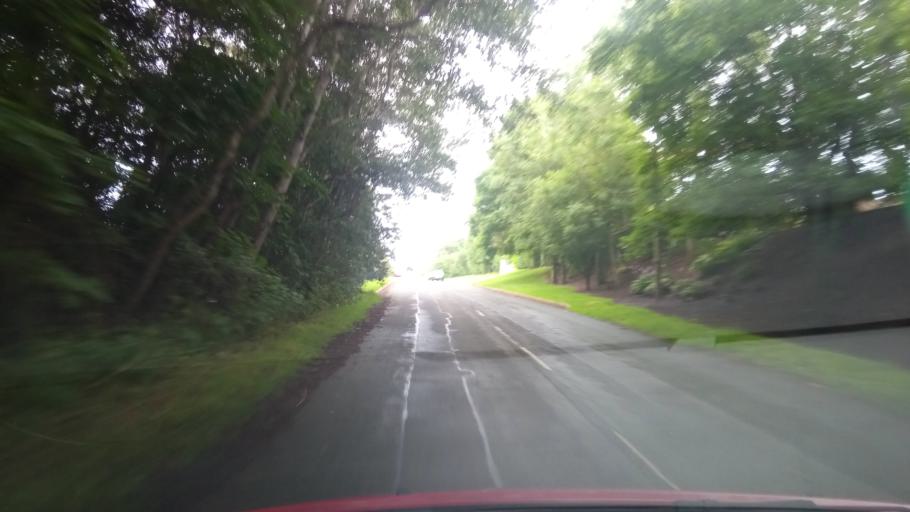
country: GB
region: Scotland
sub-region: The Scottish Borders
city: Newtown St Boswells
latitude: 55.5950
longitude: -2.6975
